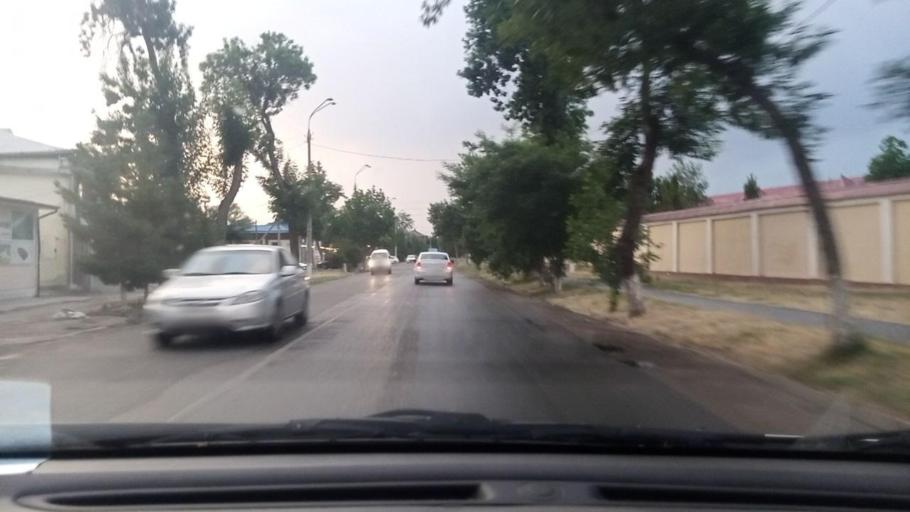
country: UZ
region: Toshkent Shahri
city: Tashkent
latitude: 41.2821
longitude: 69.2851
